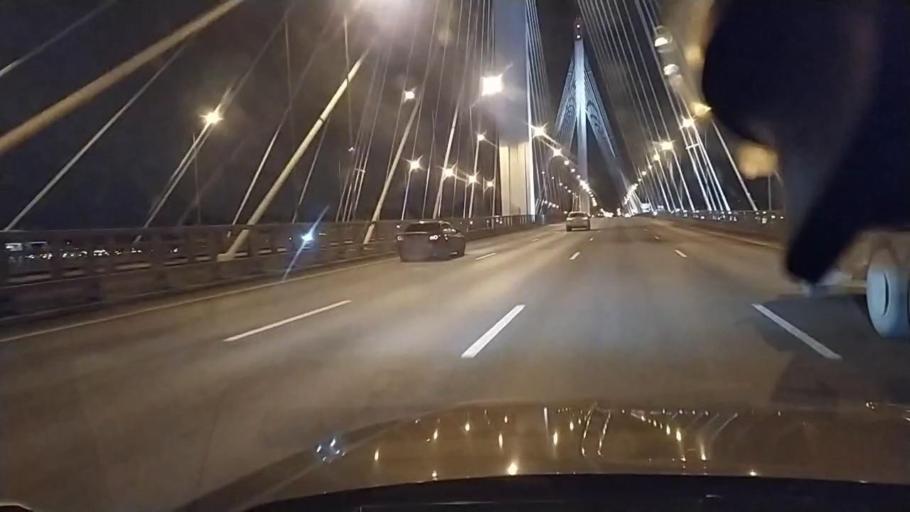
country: RU
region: St.-Petersburg
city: Staraya Derevnya
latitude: 59.9686
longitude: 30.2159
